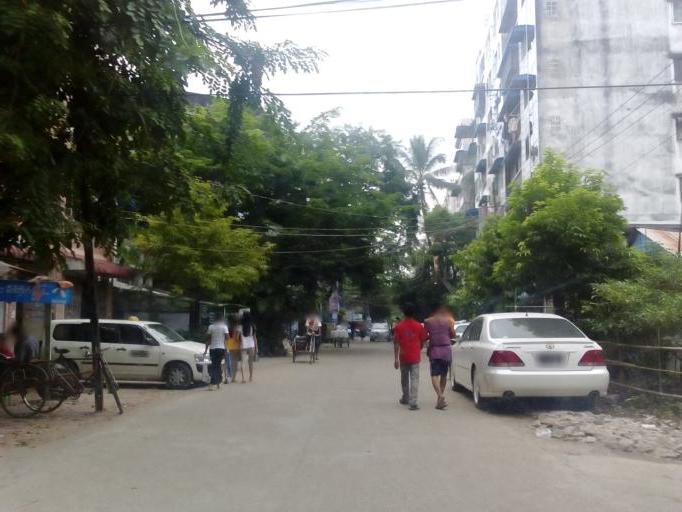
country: MM
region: Yangon
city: Yangon
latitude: 16.8021
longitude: 96.1772
